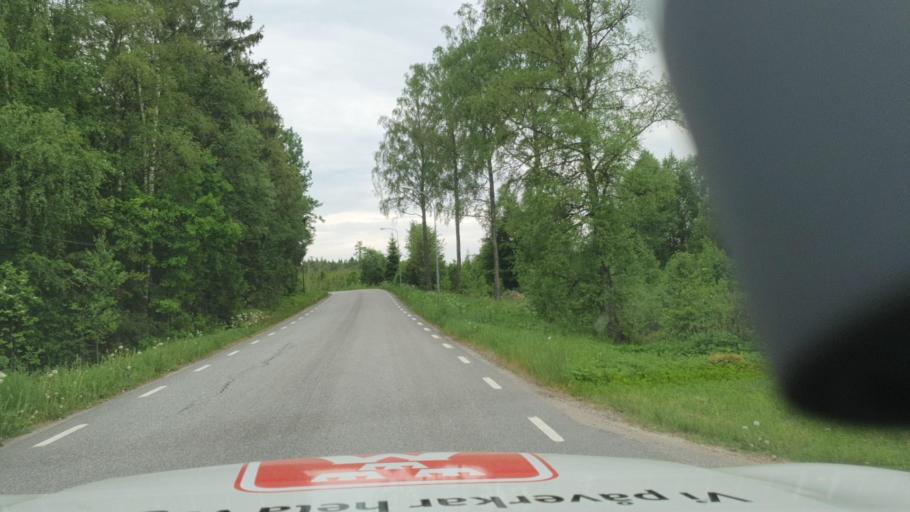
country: SE
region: Vaestra Goetaland
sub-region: Ulricehamns Kommun
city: Ulricehamn
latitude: 57.8613
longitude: 13.2766
